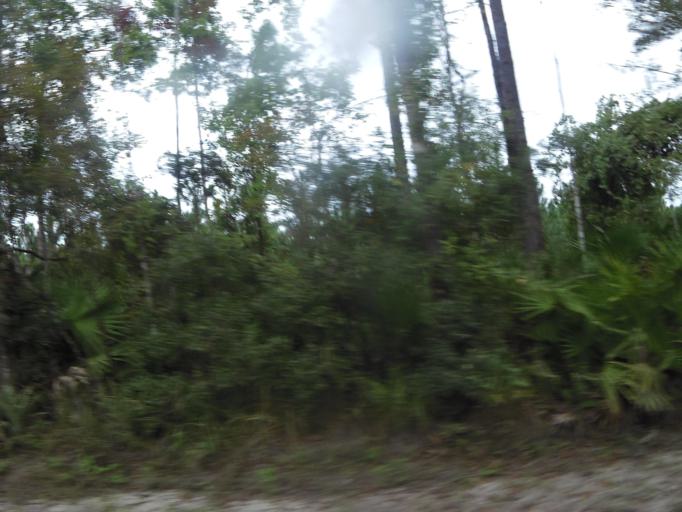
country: US
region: Florida
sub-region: Flagler County
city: Palm Coast
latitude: 29.6376
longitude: -81.3726
